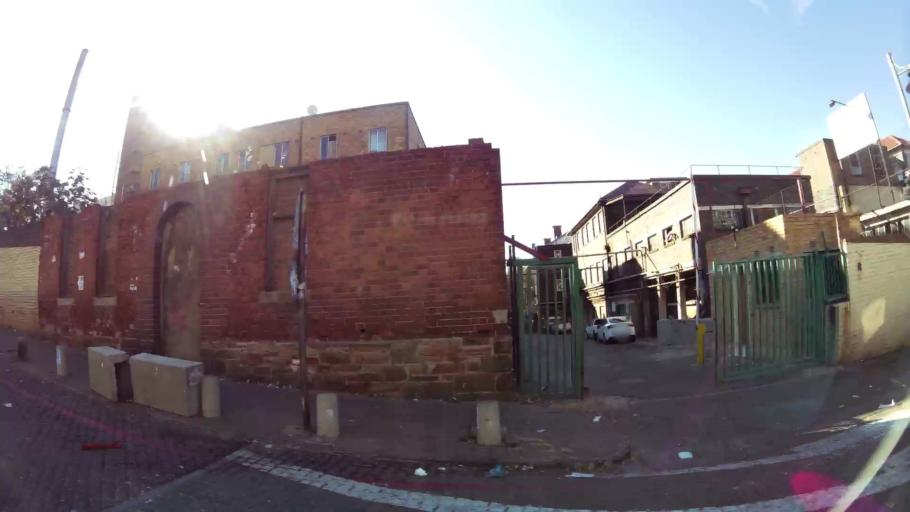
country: ZA
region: Gauteng
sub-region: City of Johannesburg Metropolitan Municipality
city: Johannesburg
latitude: -26.1915
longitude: 28.0437
